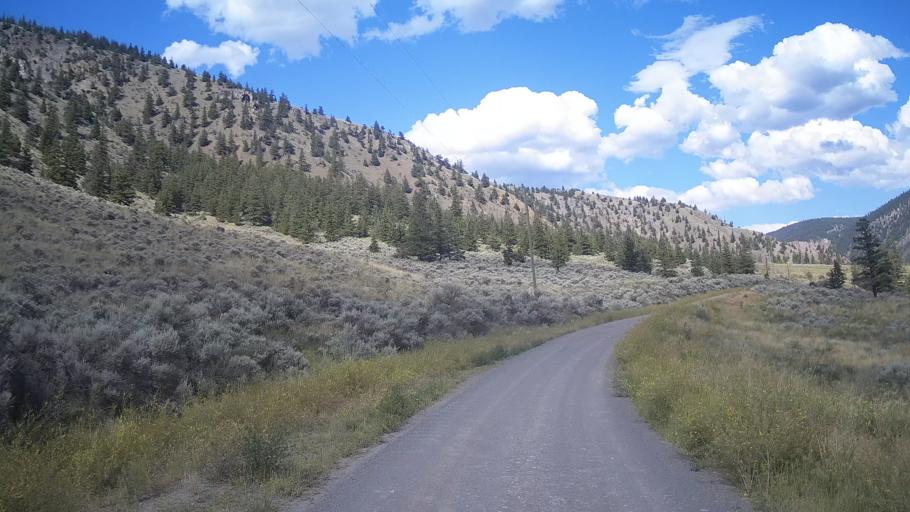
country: CA
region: British Columbia
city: Lillooet
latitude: 51.2191
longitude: -122.0926
